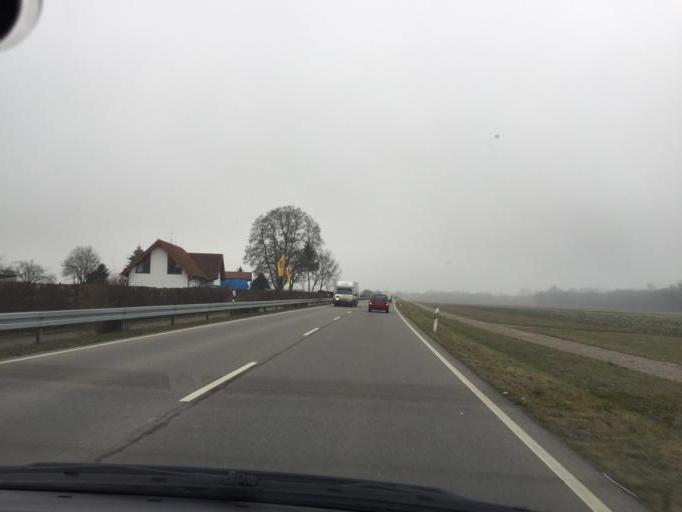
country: DE
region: Baden-Wuerttemberg
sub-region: Freiburg Region
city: Breisach am Rhein
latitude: 48.0127
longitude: 7.6154
